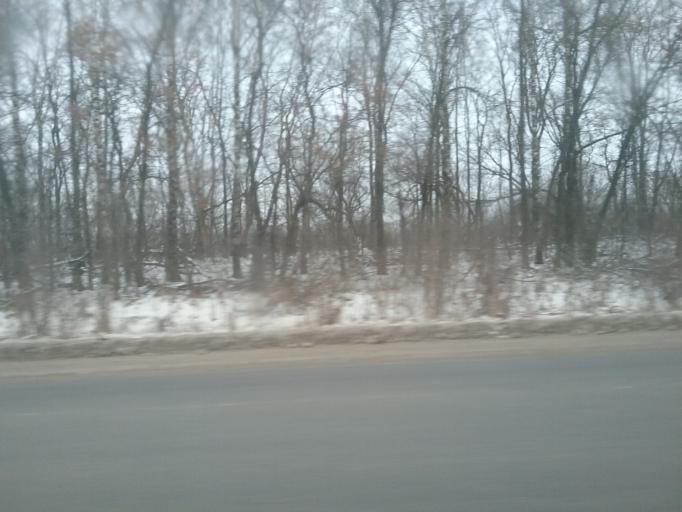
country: RU
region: Tula
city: Bolokhovo
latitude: 54.0486
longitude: 37.8362
